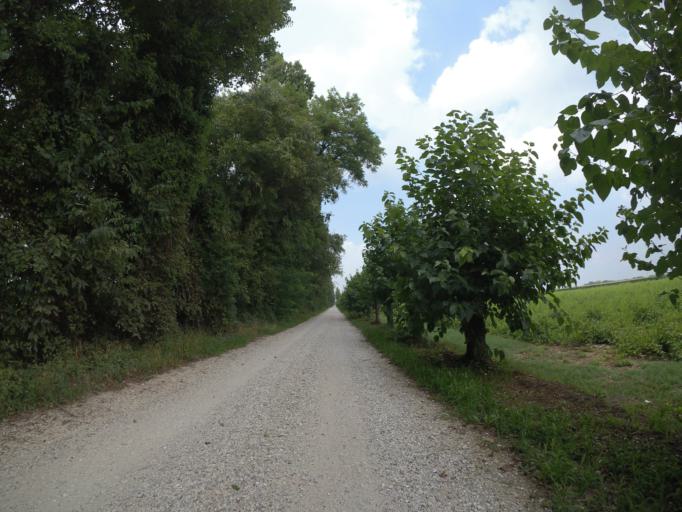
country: IT
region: Friuli Venezia Giulia
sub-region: Provincia di Udine
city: Sedegliano
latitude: 46.0023
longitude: 13.0107
